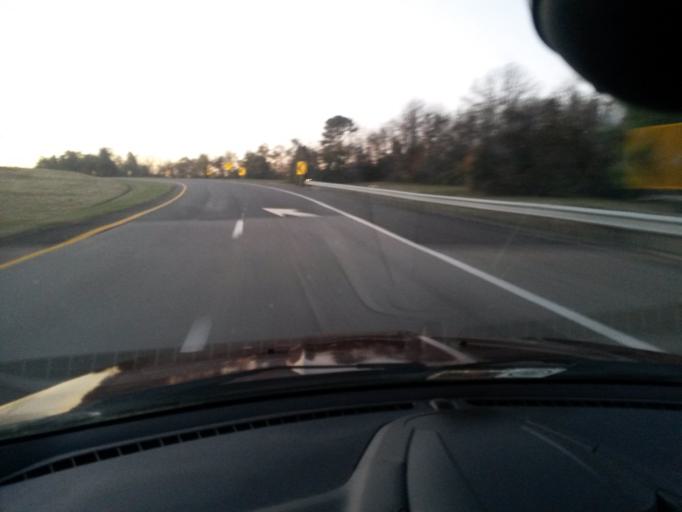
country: US
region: Virginia
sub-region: Roanoke County
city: Hollins
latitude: 37.3405
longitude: -79.9978
